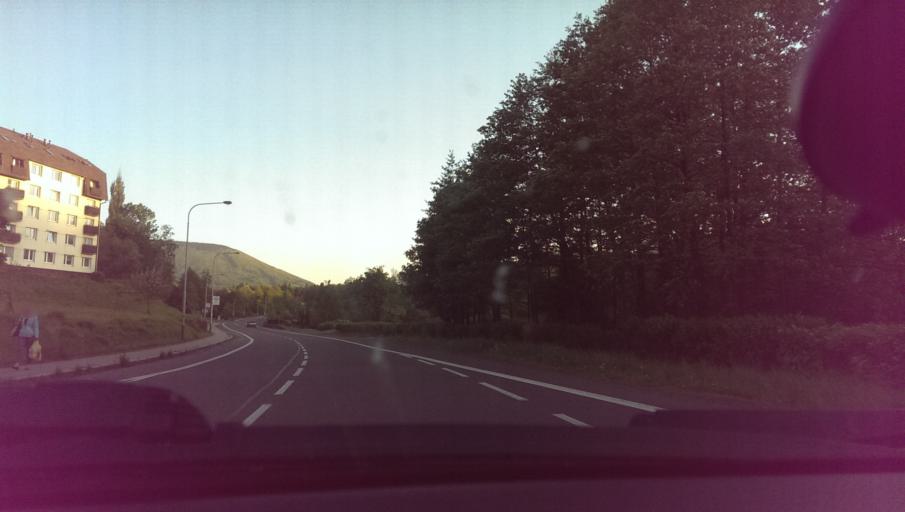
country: CZ
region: Moravskoslezsky
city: Frenstat pod Radhostem
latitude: 49.5392
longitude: 18.2049
